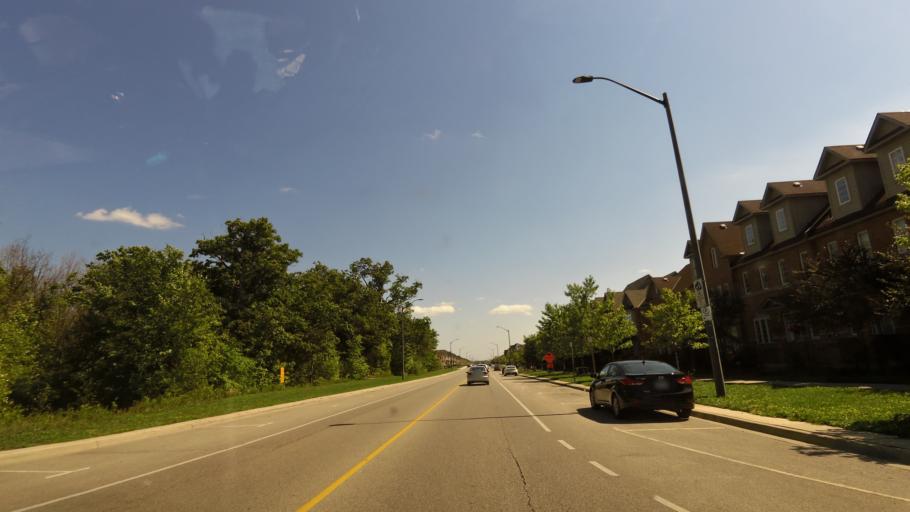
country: CA
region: Ontario
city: Mississauga
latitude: 43.5579
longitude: -79.7405
